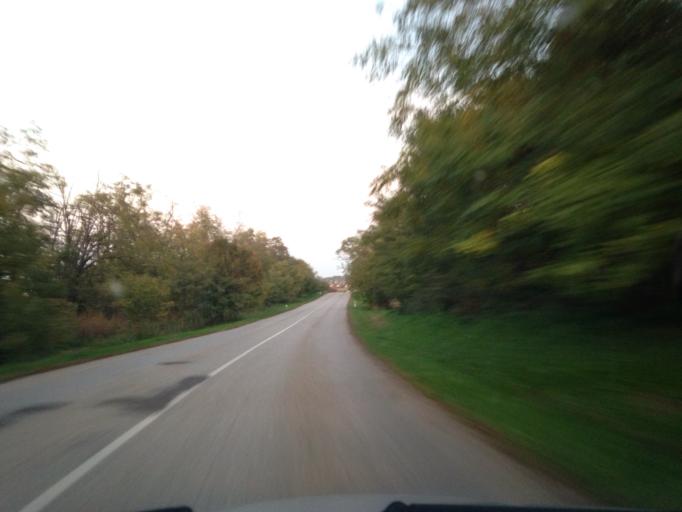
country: SK
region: Nitriansky
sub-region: Okres Komarno
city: Hurbanovo
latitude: 47.8331
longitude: 18.2400
